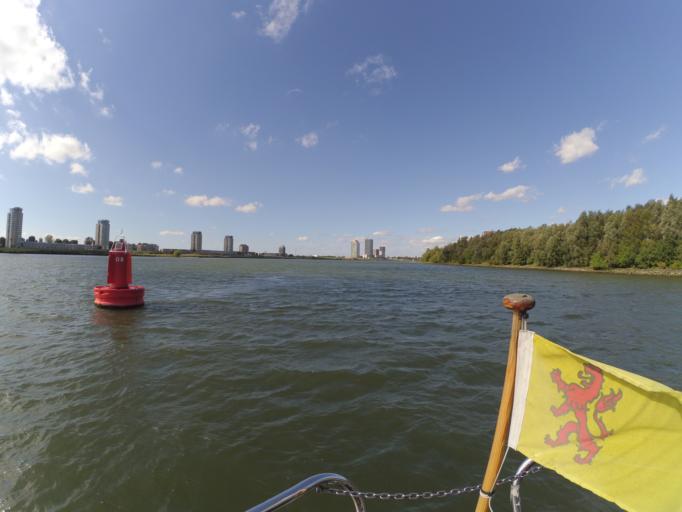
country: NL
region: South Holland
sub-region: Gemeente Spijkenisse
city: Spijkenisse
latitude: 51.8468
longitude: 4.3631
